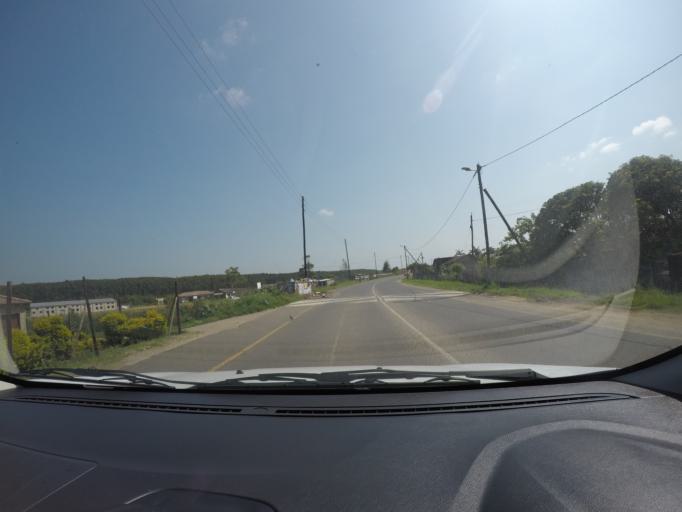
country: ZA
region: KwaZulu-Natal
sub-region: uThungulu District Municipality
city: eSikhawini
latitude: -28.8896
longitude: 31.8814
